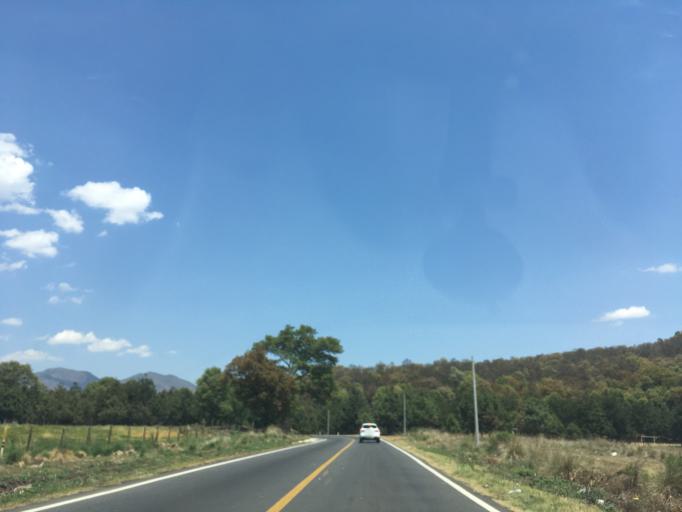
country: MX
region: Michoacan
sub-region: Chilchota
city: Tacuro (Santa Maria Tacuro)
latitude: 19.8210
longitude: -102.0272
